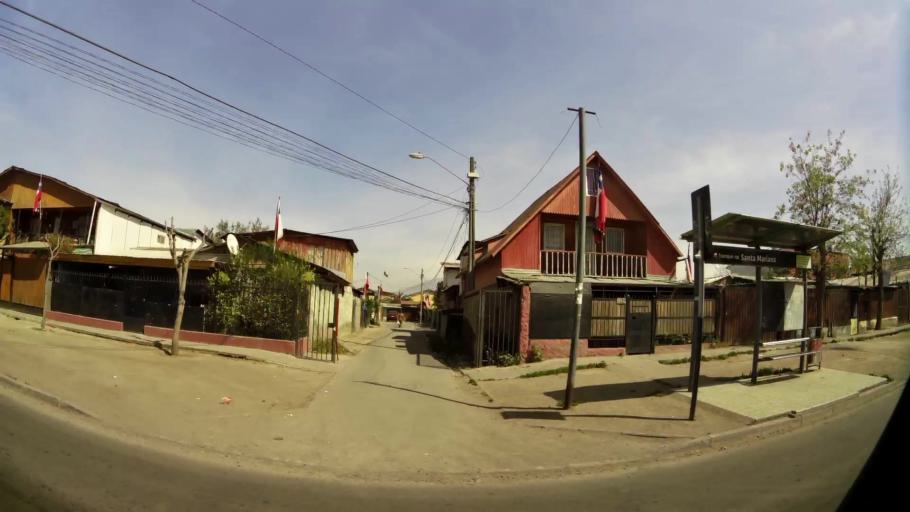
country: CL
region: Santiago Metropolitan
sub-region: Provincia de Santiago
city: Lo Prado
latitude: -33.4326
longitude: -70.7708
